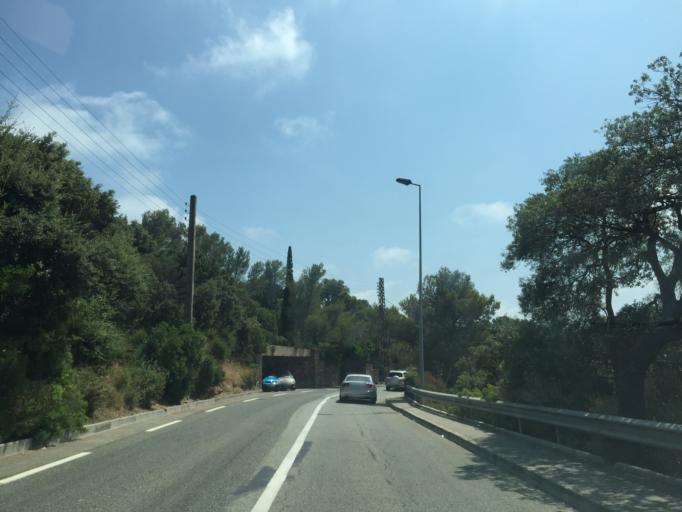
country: FR
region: Provence-Alpes-Cote d'Azur
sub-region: Departement du Var
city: Saint-Raphael
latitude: 43.4276
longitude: 6.8713
